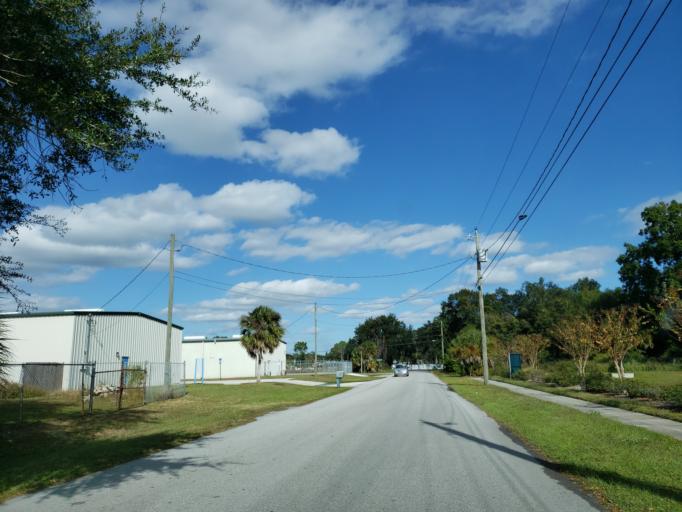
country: US
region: Florida
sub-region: Polk County
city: Lakeland Highlands
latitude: 27.9594
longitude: -81.9584
